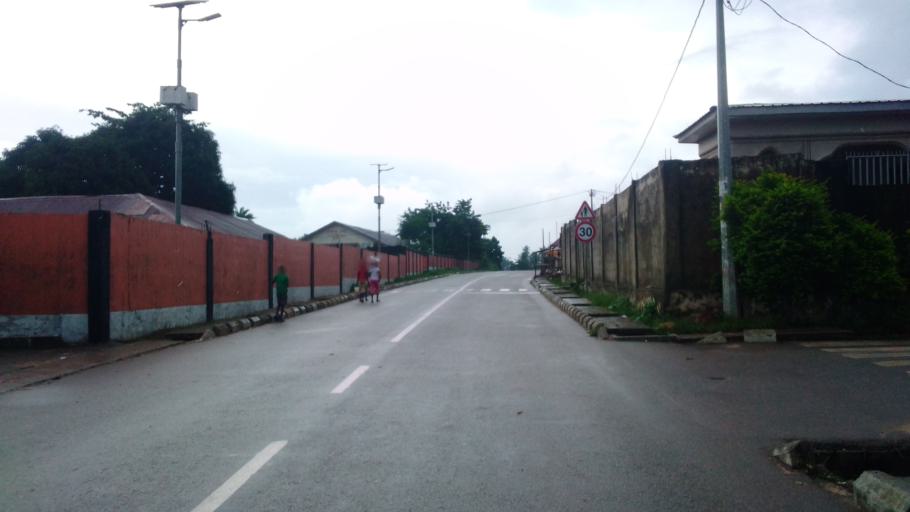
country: SL
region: Northern Province
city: Lunsar
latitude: 8.6826
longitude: -12.5343
